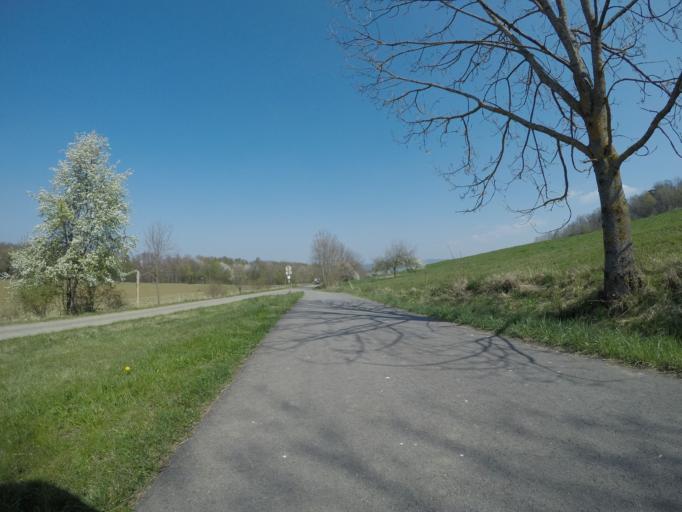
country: DE
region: Baden-Wuerttemberg
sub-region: Tuebingen Region
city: Gomaringen
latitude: 48.4598
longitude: 9.1444
